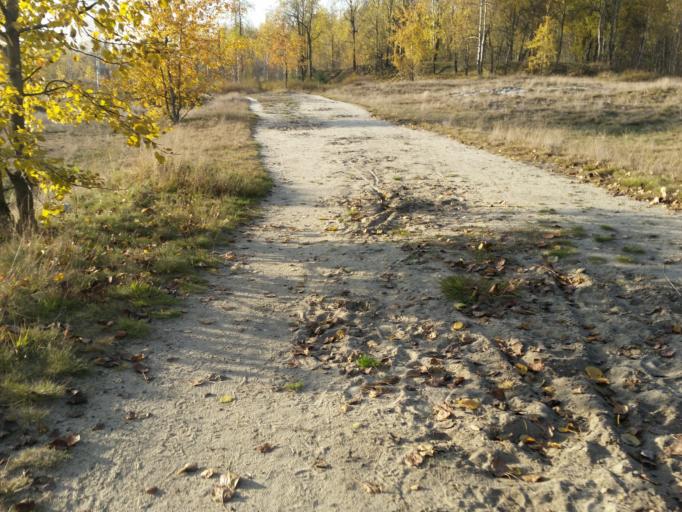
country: PL
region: Silesian Voivodeship
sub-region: Sosnowiec
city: Sosnowiec
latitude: 50.2687
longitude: 19.1164
